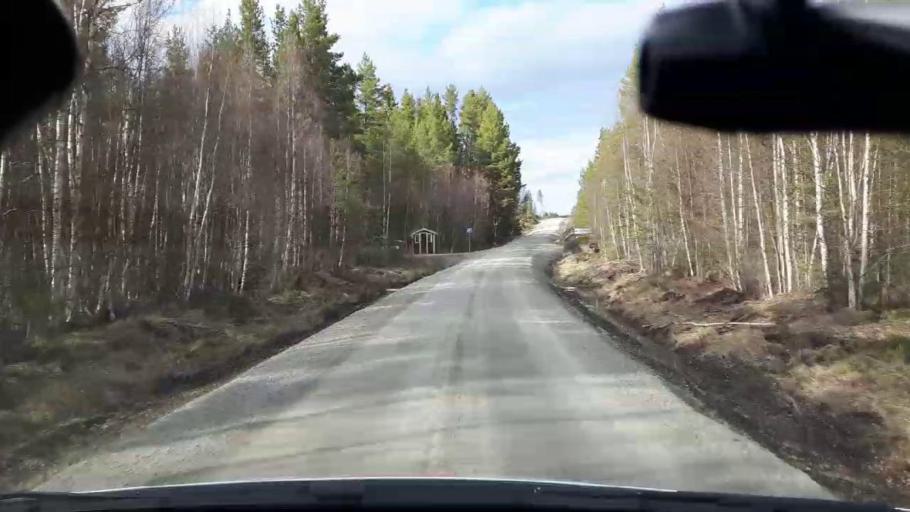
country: SE
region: Jaemtland
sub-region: Bergs Kommun
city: Hoverberg
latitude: 62.9228
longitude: 14.6411
